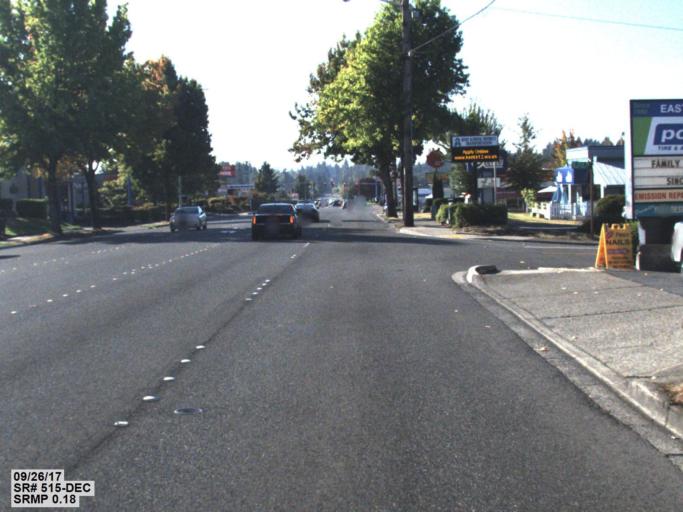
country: US
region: Washington
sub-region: King County
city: Kent
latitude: 47.3751
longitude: -122.2024
